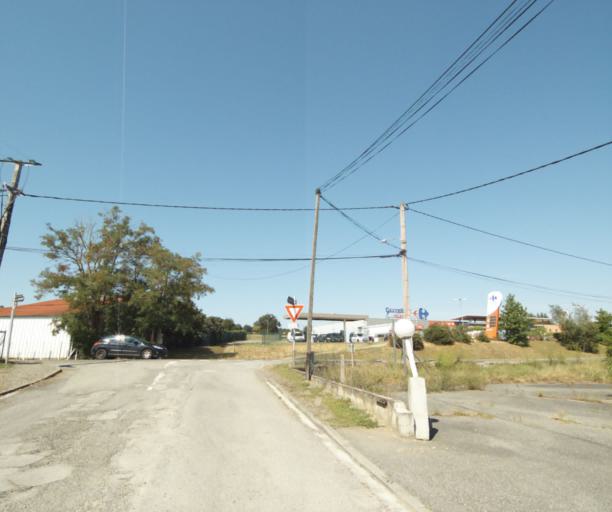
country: FR
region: Midi-Pyrenees
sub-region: Departement de l'Ariege
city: Lezat-sur-Leze
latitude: 43.2817
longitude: 1.3479
